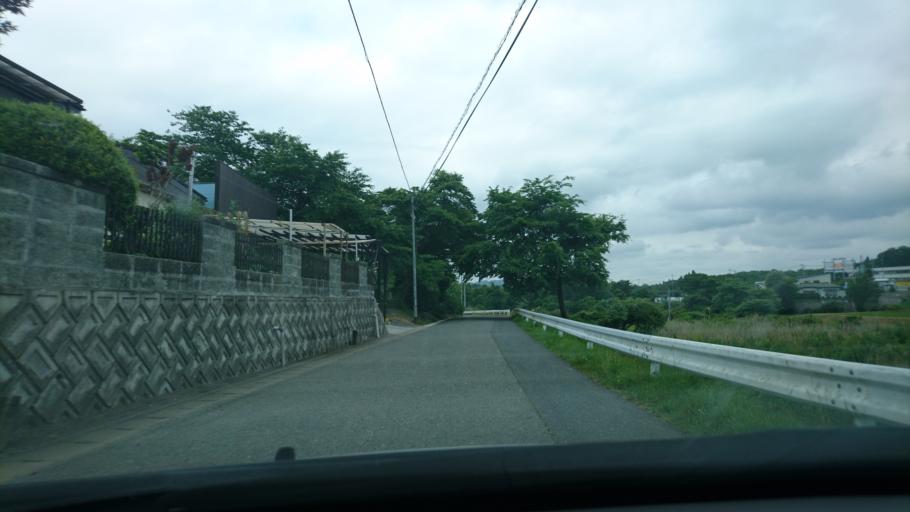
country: JP
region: Iwate
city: Ichinoseki
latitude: 38.9123
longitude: 141.1547
